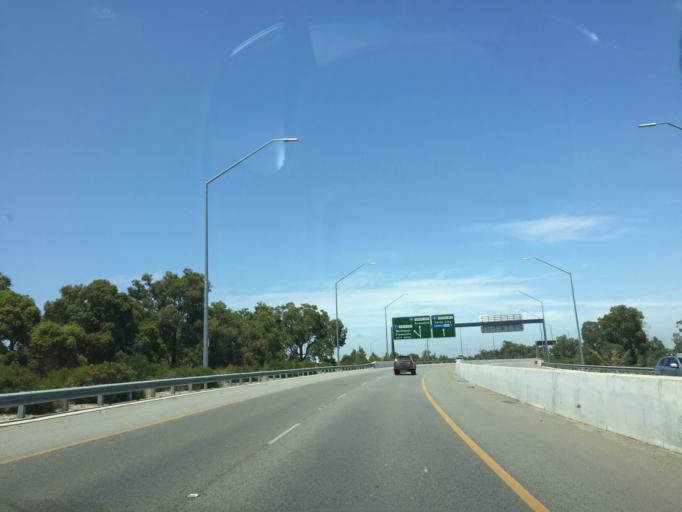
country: AU
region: Western Australia
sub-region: Belmont
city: Kewdale
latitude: -31.9609
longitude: 115.9673
